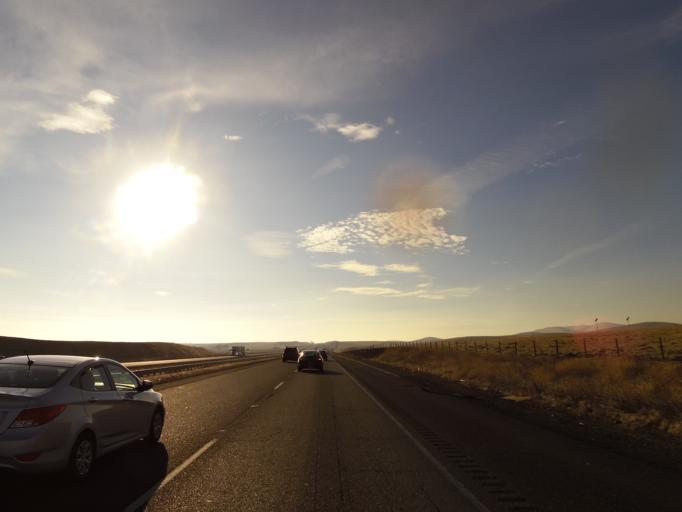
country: US
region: California
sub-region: Merced County
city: Gustine
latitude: 37.1851
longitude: -121.0685
